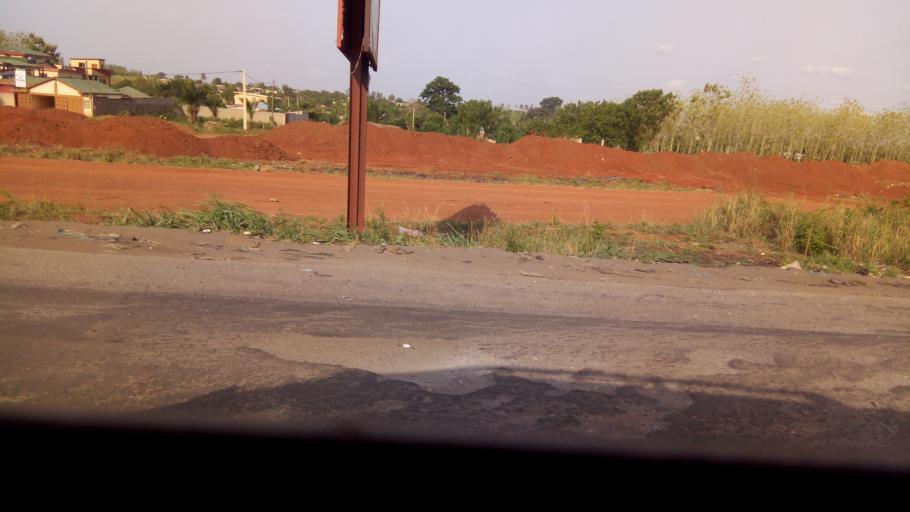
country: TG
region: Maritime
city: Tsevie
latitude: 6.3749
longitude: 1.2054
